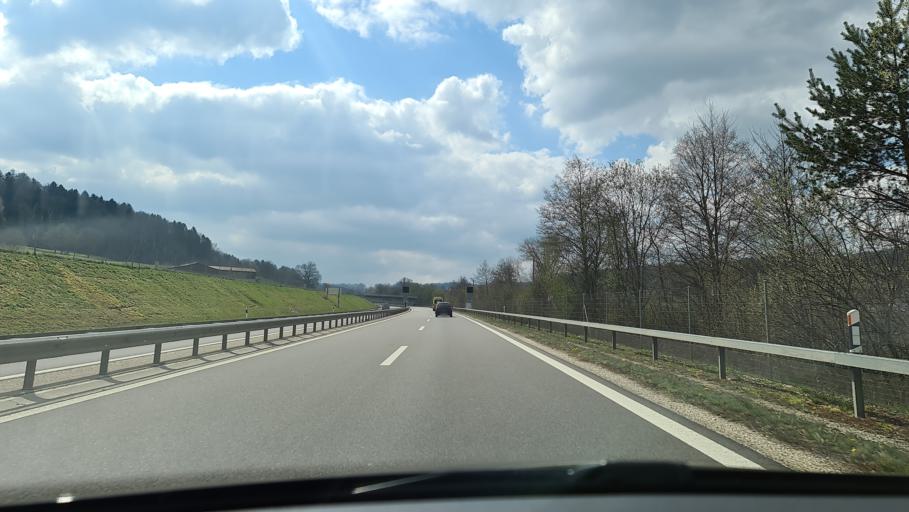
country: CH
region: Jura
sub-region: Delemont District
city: Courtetelle
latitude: 47.3590
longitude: 7.3121
